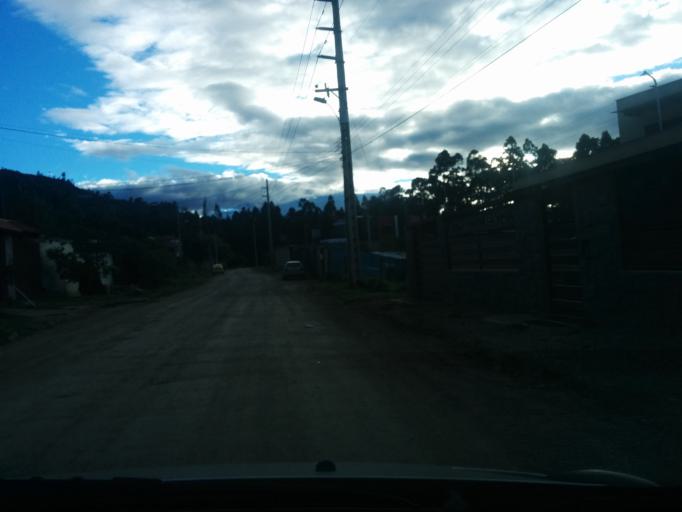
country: EC
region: Azuay
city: Cuenca
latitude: -2.8805
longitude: -78.9463
